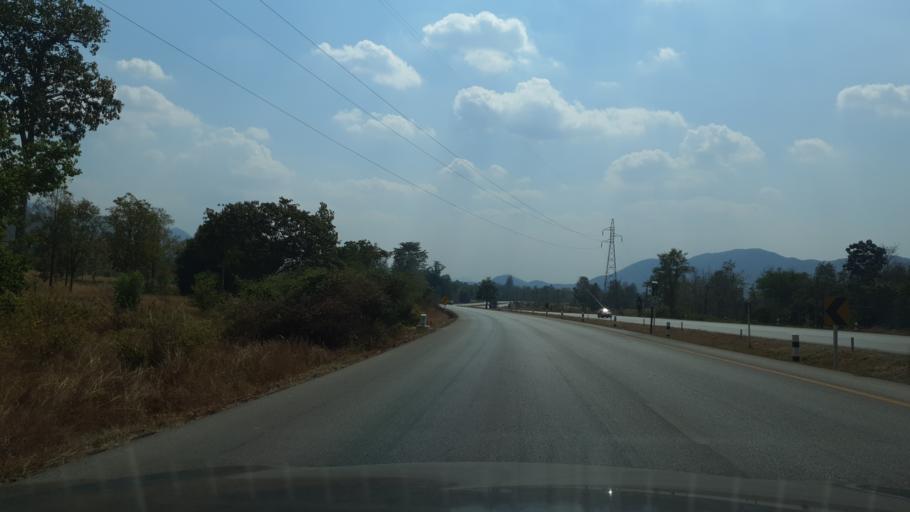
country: TH
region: Lampang
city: Mae Phrik
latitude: 17.3816
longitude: 99.1481
